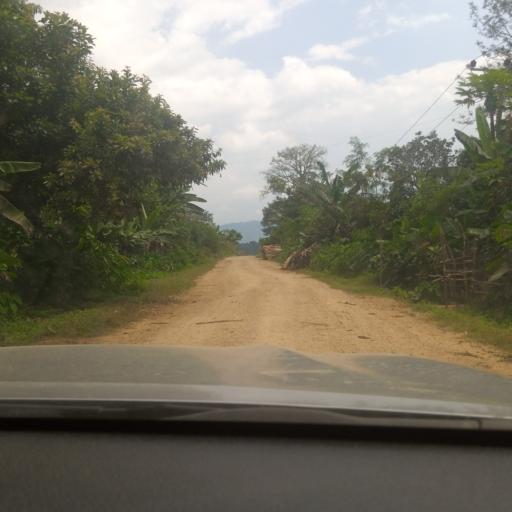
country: ET
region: Southern Nations, Nationalities, and People's Region
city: Tippi
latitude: 7.1338
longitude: 35.4252
